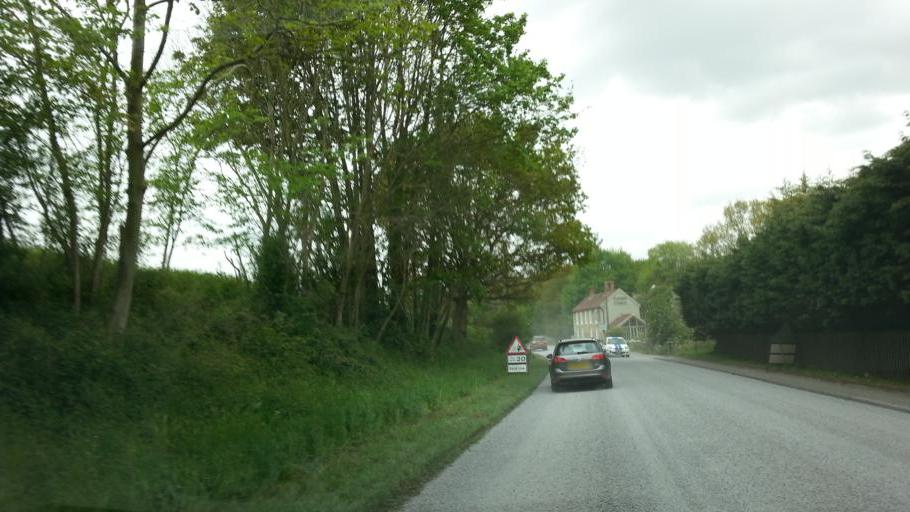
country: GB
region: England
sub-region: Suffolk
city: Bury St Edmunds
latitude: 52.2046
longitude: 0.7561
